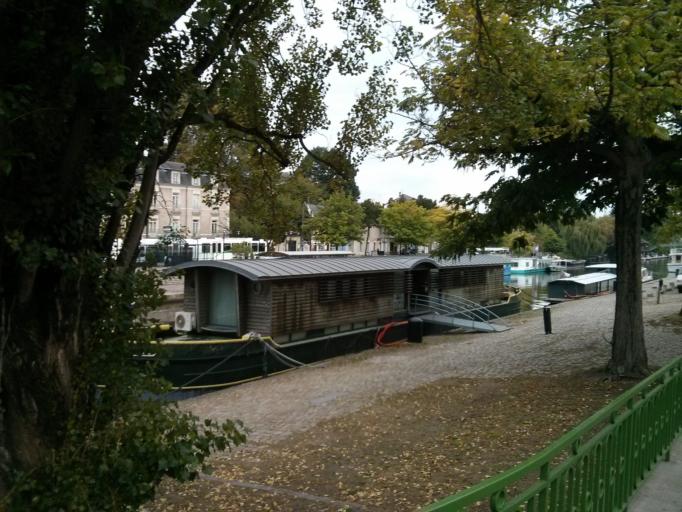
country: FR
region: Pays de la Loire
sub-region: Departement de la Loire-Atlantique
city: Nantes
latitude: 47.2230
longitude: -1.5525
